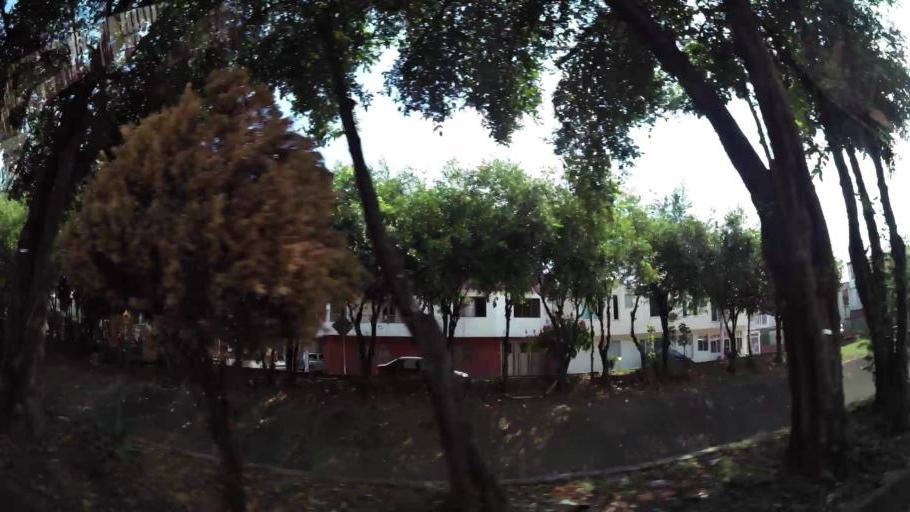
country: CO
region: Valle del Cauca
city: Cali
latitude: 3.4929
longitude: -76.4986
